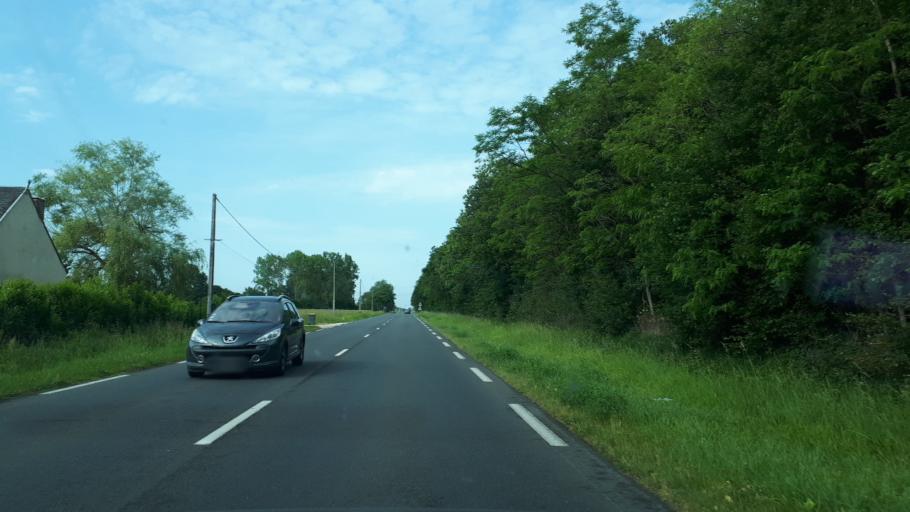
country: FR
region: Centre
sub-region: Departement d'Indre-et-Loire
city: Monnaie
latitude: 47.4867
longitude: 0.7712
